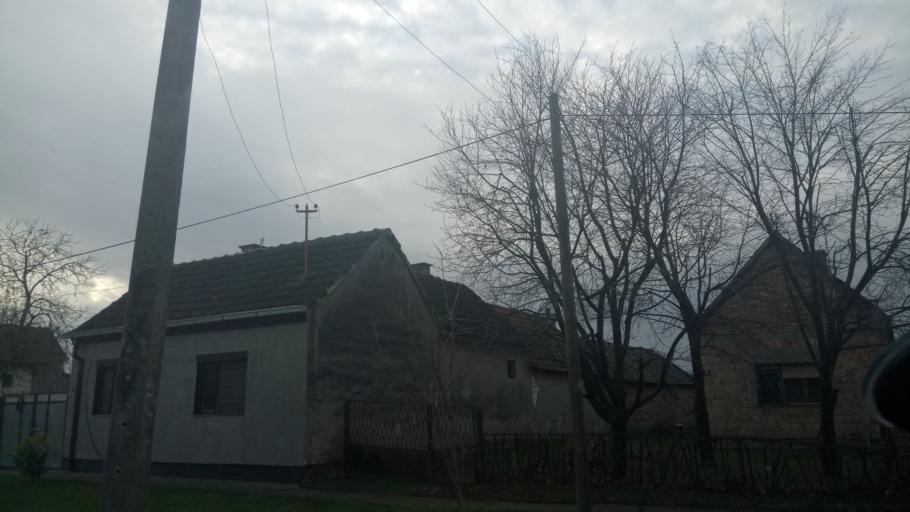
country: RS
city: Vojka
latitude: 44.9334
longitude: 20.1539
